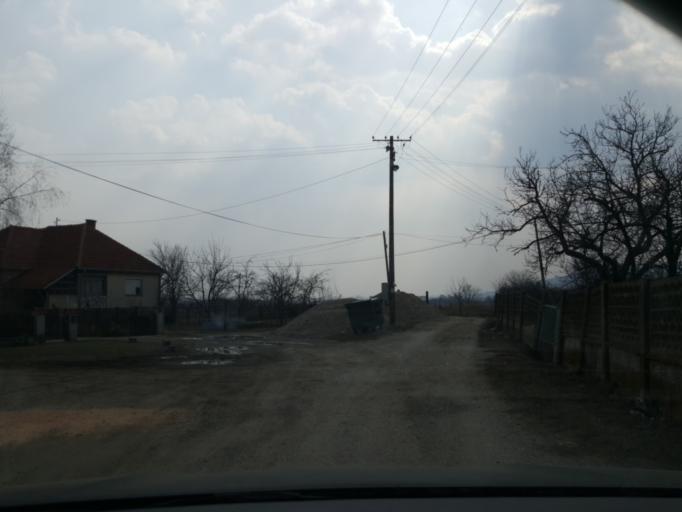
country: RS
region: Central Serbia
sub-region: Nisavski Okrug
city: Aleksinac
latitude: 43.4477
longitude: 21.7911
